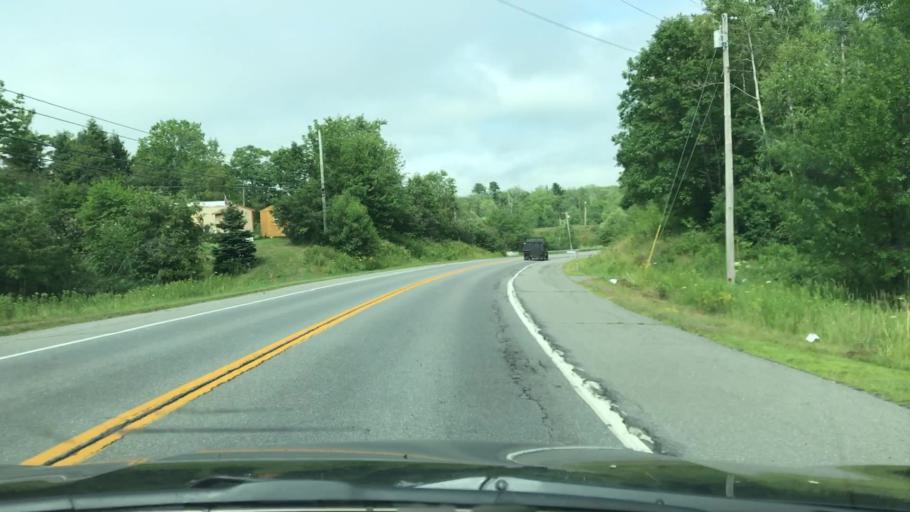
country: US
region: Maine
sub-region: Waldo County
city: Stockton Springs
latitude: 44.4681
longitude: -68.8998
